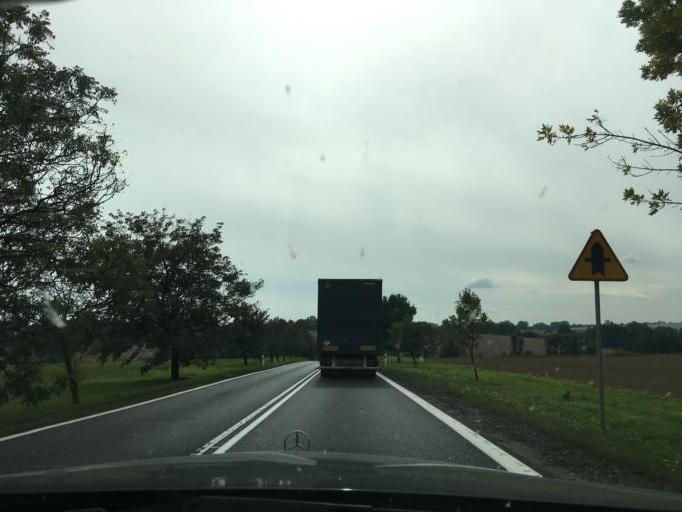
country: PL
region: Lower Silesian Voivodeship
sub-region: Powiat dzierzoniowski
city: Niemcza
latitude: 50.7177
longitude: 16.8253
